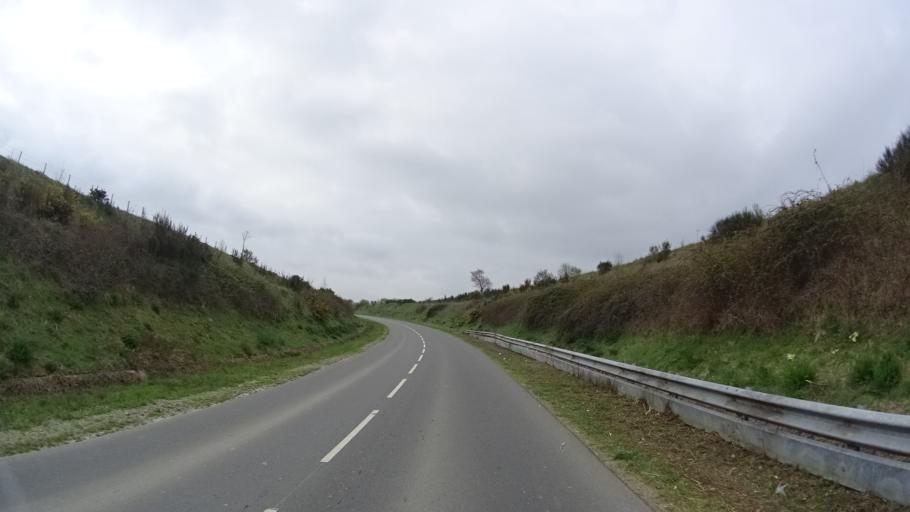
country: FR
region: Brittany
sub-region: Departement d'Ille-et-Vilaine
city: La Chapelle-Thouarault
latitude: 48.1305
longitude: -1.8551
